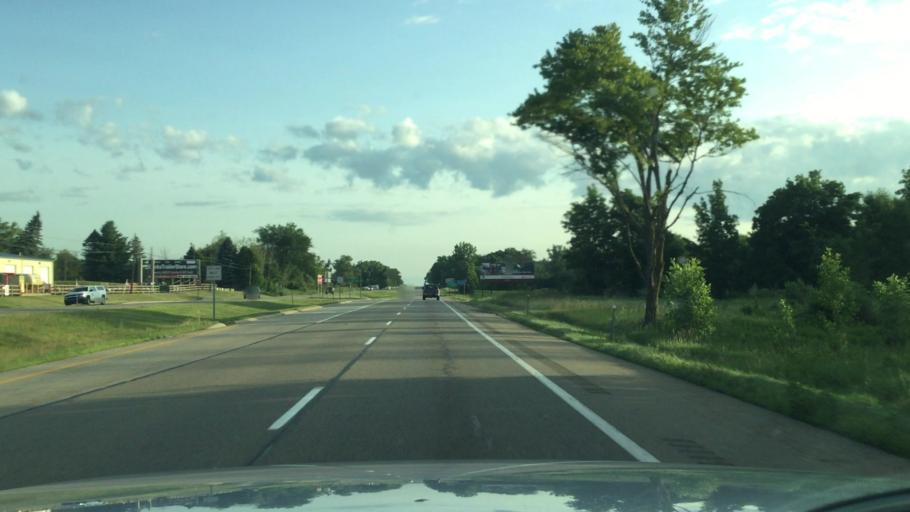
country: US
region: Michigan
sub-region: Clinton County
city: Saint Johns
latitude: 43.0984
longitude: -84.5633
